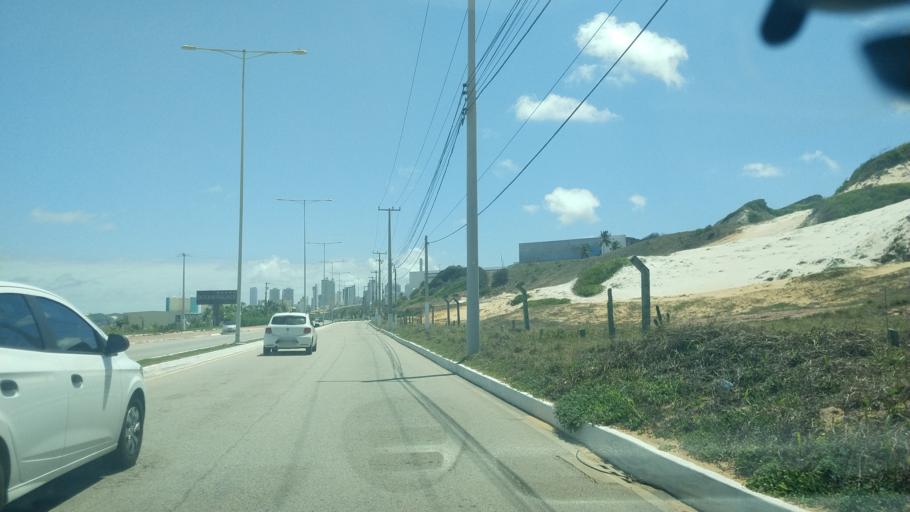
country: BR
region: Rio Grande do Norte
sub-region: Natal
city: Natal
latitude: -5.8584
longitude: -35.1816
